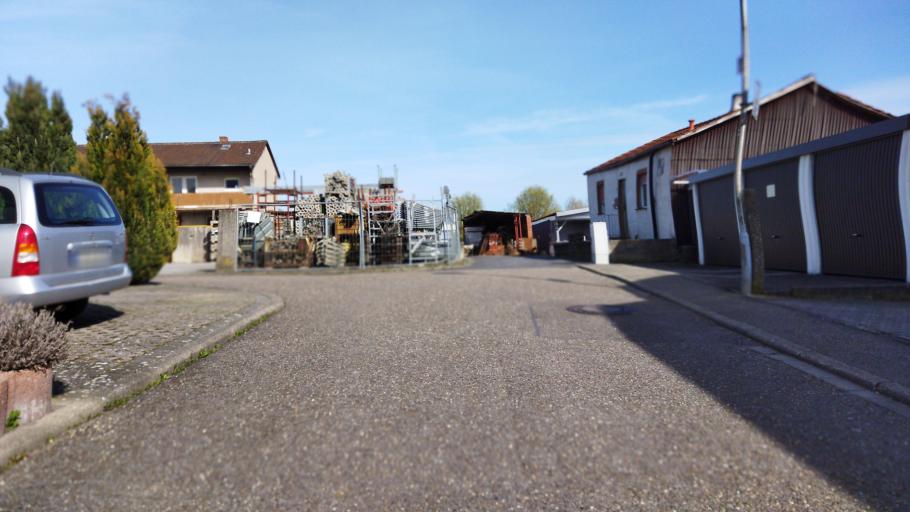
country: DE
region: Baden-Wuerttemberg
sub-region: Regierungsbezirk Stuttgart
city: Eppingen
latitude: 49.1391
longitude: 8.9143
